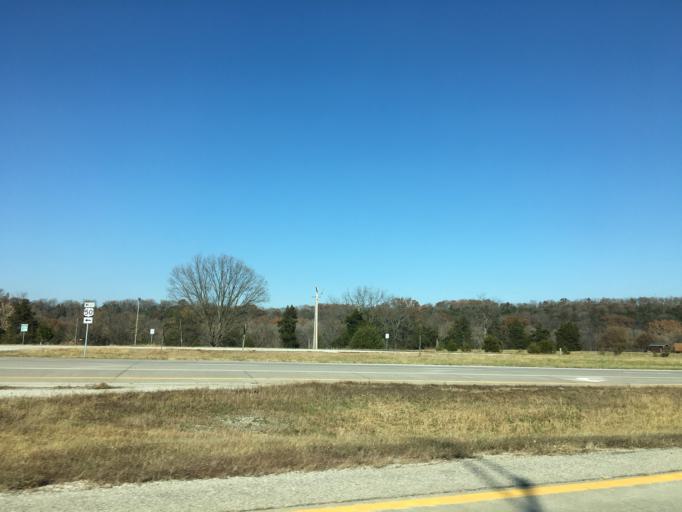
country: US
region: Missouri
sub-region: Osage County
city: Linn
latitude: 38.4934
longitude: -91.9962
